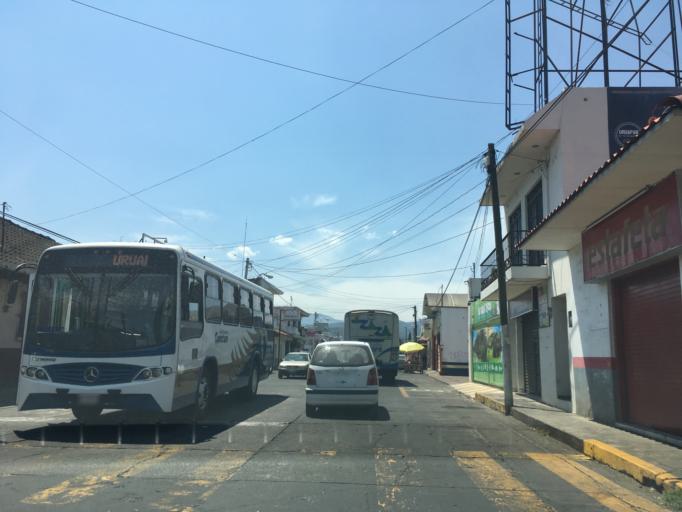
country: MX
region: Michoacan
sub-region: Uruapan
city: Uruapan
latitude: 19.4162
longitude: -102.0564
